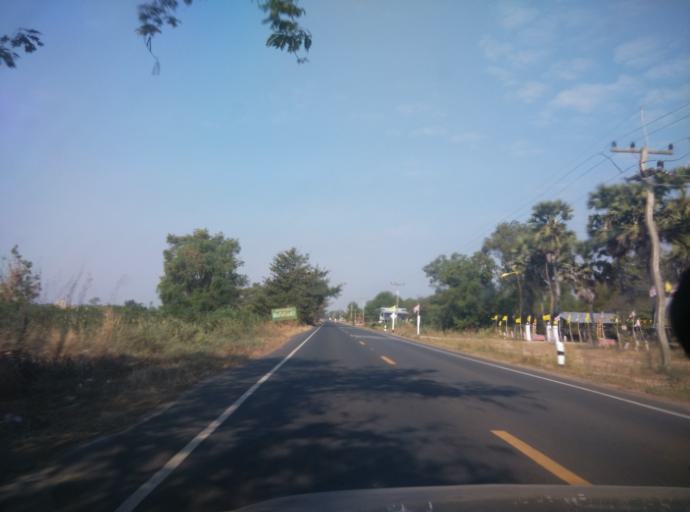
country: TH
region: Sisaket
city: Si Sa Ket
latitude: 15.1141
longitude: 104.2661
